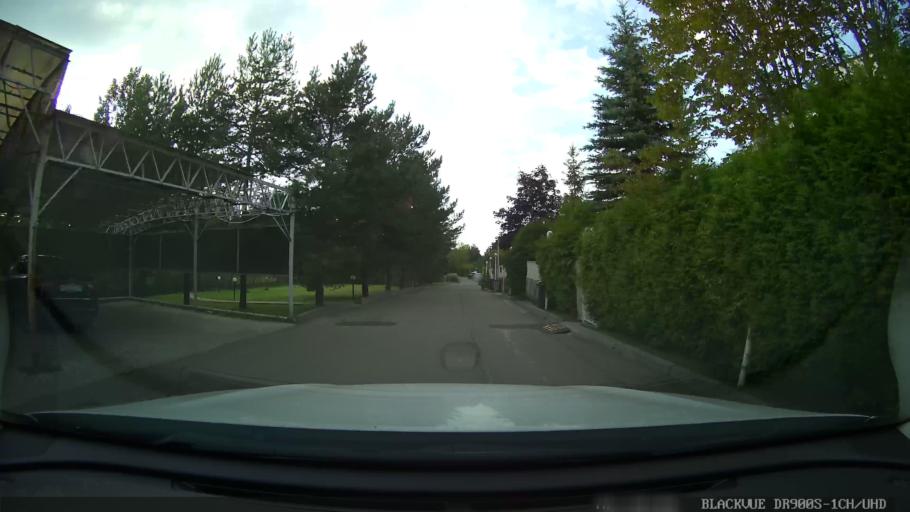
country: RU
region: Moskovskaya
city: Nemchinovka
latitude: 55.7404
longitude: 37.3391
